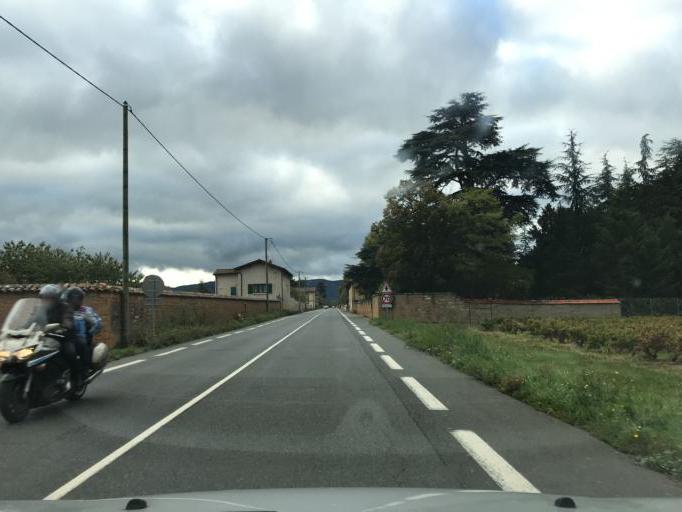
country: FR
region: Rhone-Alpes
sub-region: Departement du Rhone
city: Denice
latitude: 45.9956
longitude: 4.6698
